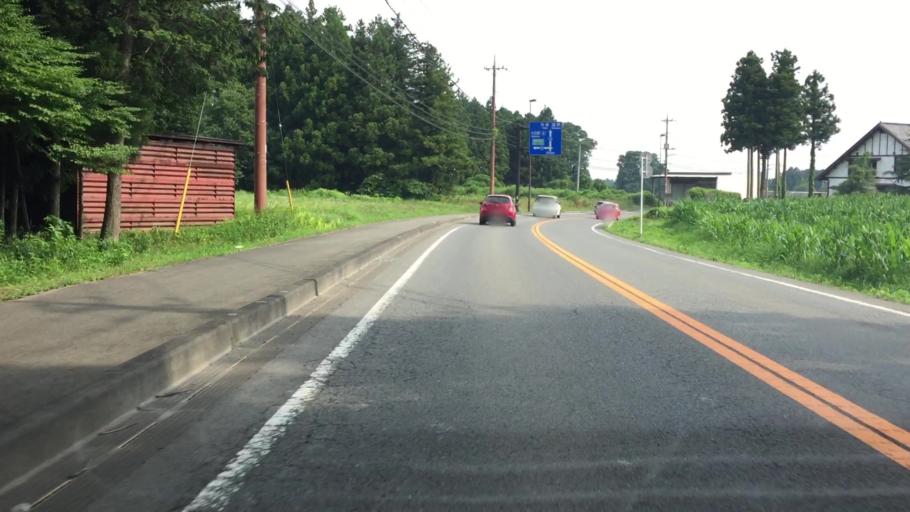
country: JP
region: Tochigi
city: Kuroiso
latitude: 36.9952
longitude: 139.9426
